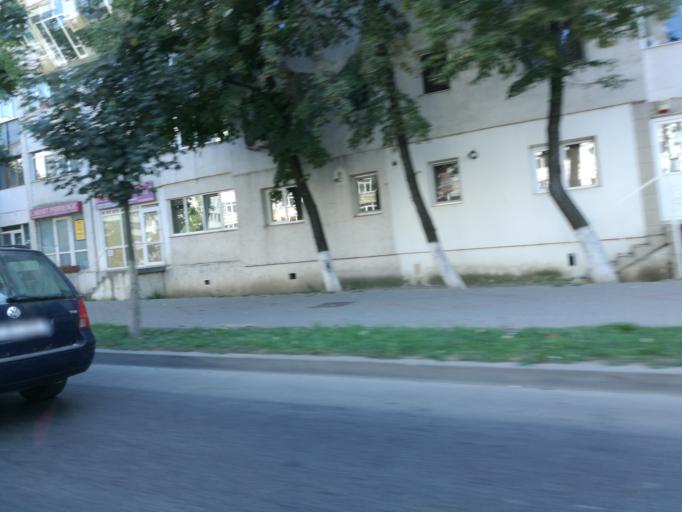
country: RO
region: Iasi
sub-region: Municipiul Iasi
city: Iasi
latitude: 47.1691
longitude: 27.5653
